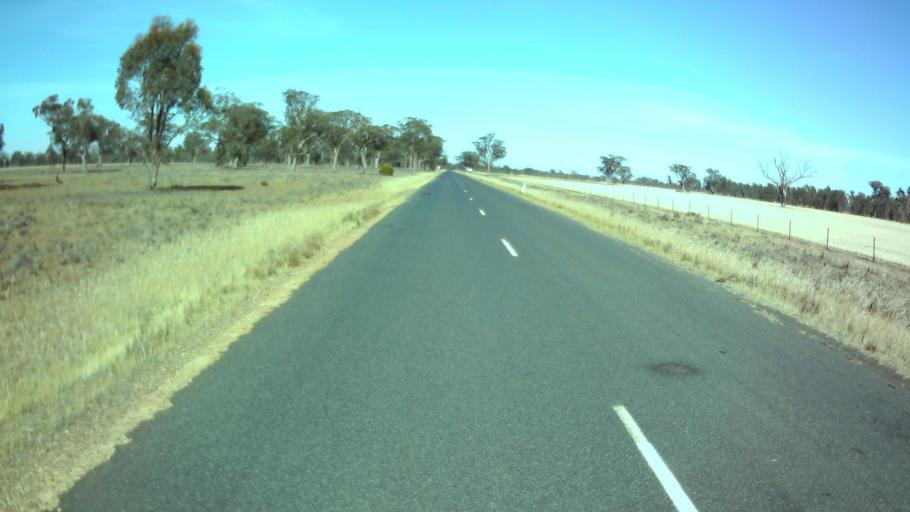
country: AU
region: New South Wales
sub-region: Weddin
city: Grenfell
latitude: -34.1367
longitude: 147.7645
